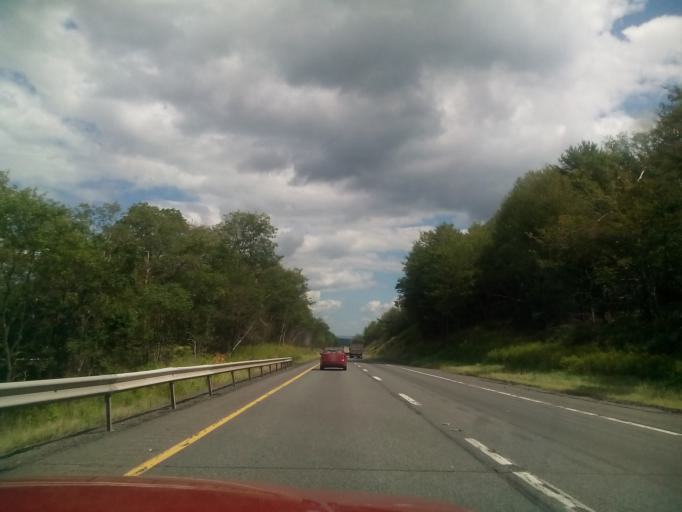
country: US
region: Pennsylvania
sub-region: Monroe County
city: Tannersville
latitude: 41.0643
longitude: -75.3493
